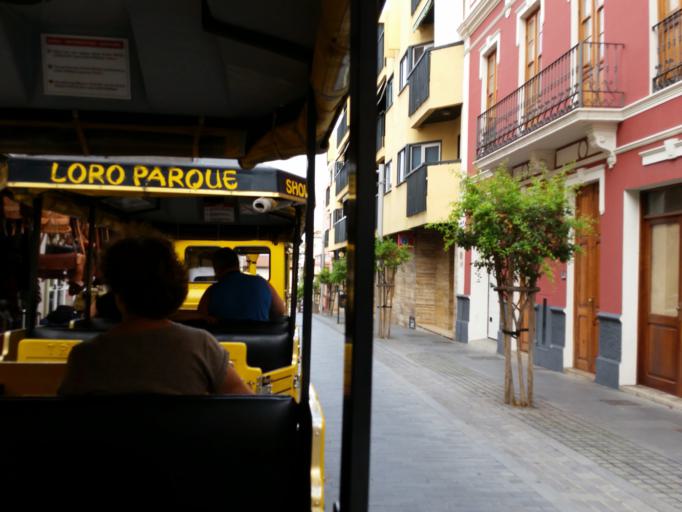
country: ES
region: Canary Islands
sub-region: Provincia de Santa Cruz de Tenerife
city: Puerto de la Cruz
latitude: 28.4160
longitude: -16.5475
